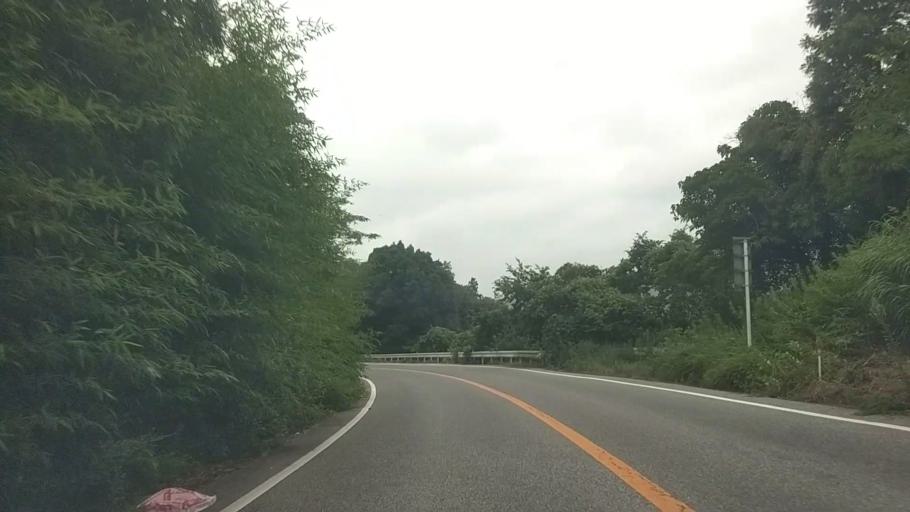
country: JP
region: Chiba
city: Kimitsu
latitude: 35.2426
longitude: 140.0065
